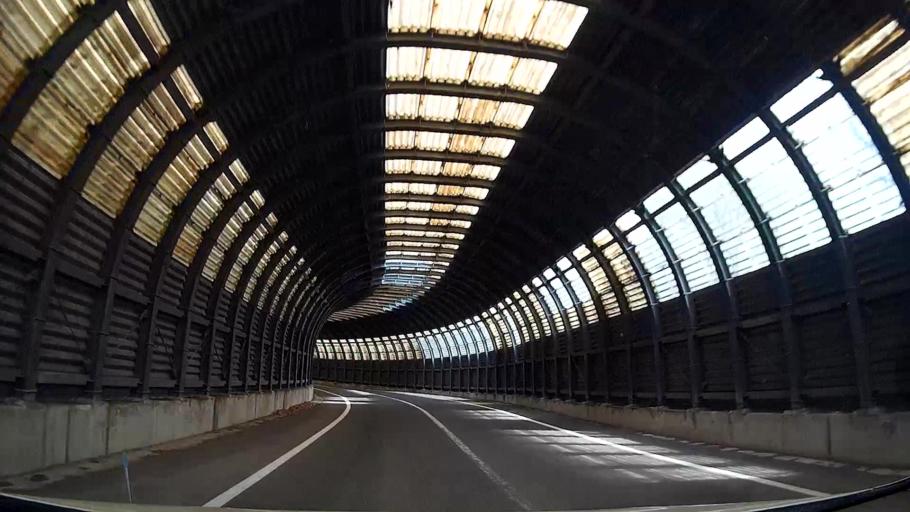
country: JP
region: Iwate
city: Shizukuishi
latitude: 39.9265
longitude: 140.9619
